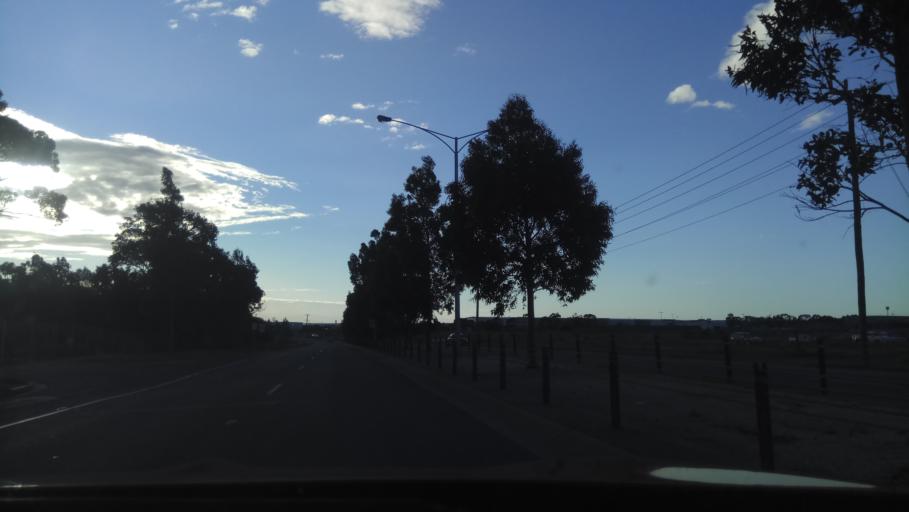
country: AU
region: Victoria
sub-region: Hobsons Bay
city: Seaholme
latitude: -37.8500
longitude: 144.8442
